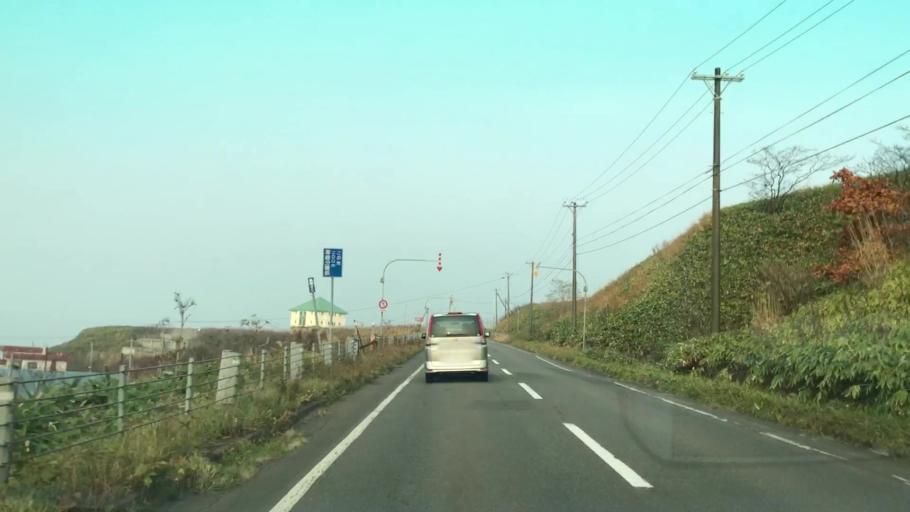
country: JP
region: Hokkaido
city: Ishikari
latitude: 43.3365
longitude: 141.4262
